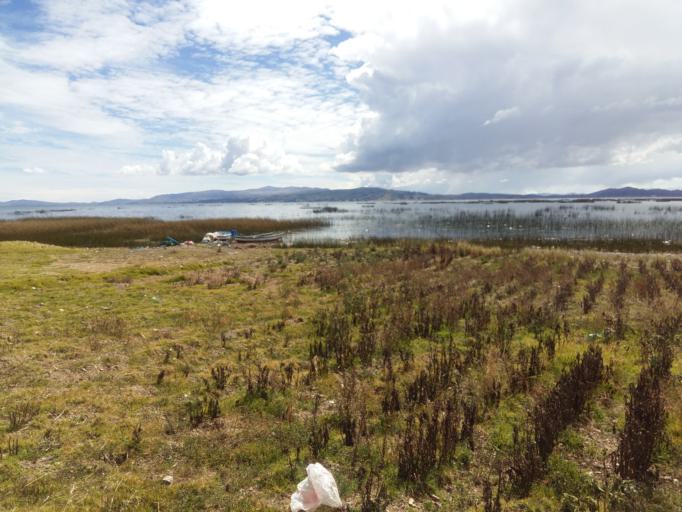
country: BO
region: La Paz
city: Batallas
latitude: -16.2818
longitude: -68.6000
